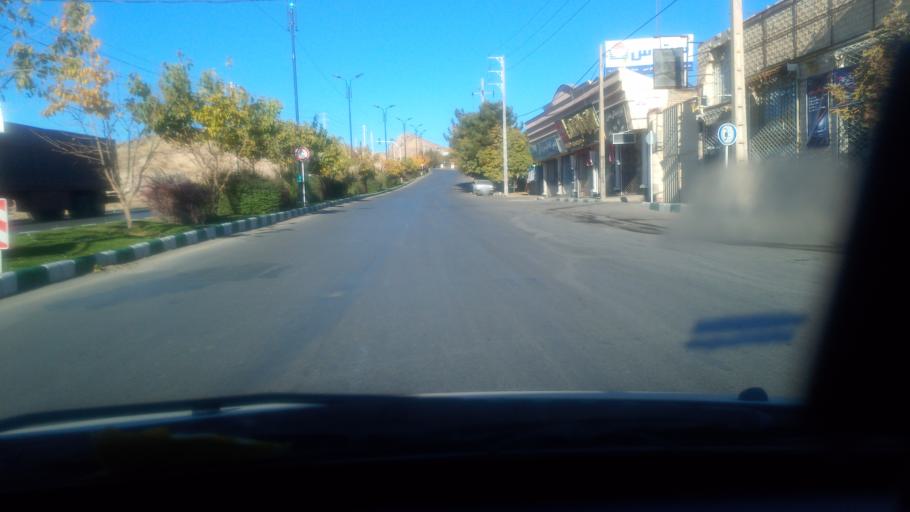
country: IR
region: Razavi Khorasan
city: Torqabeh
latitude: 36.3139
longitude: 59.3664
